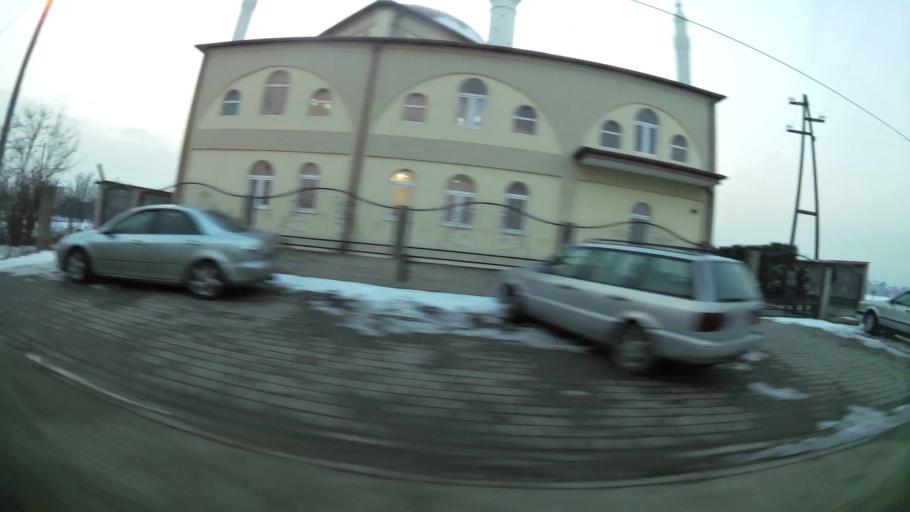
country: MK
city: Creshevo
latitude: 42.0073
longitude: 21.5175
